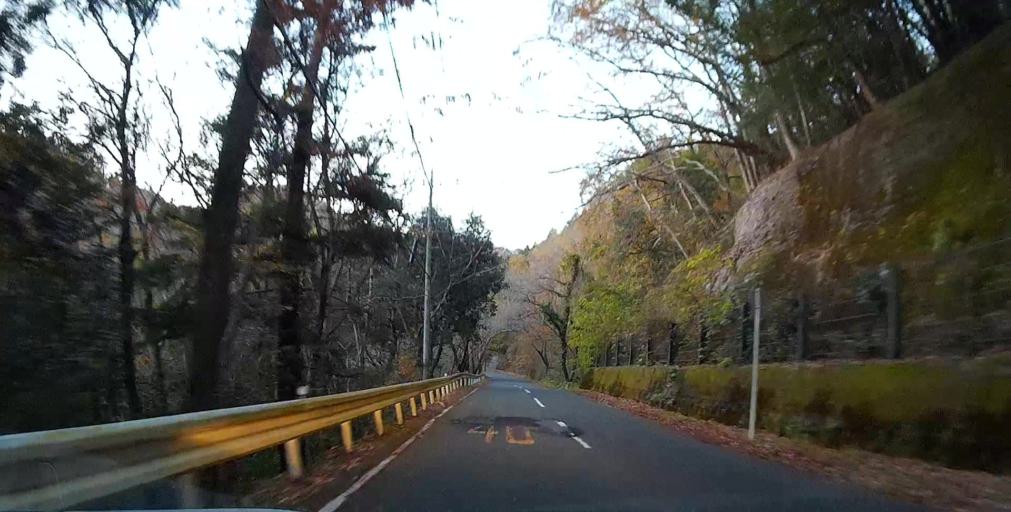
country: JP
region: Yamanashi
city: Uenohara
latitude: 35.5742
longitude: 139.1908
